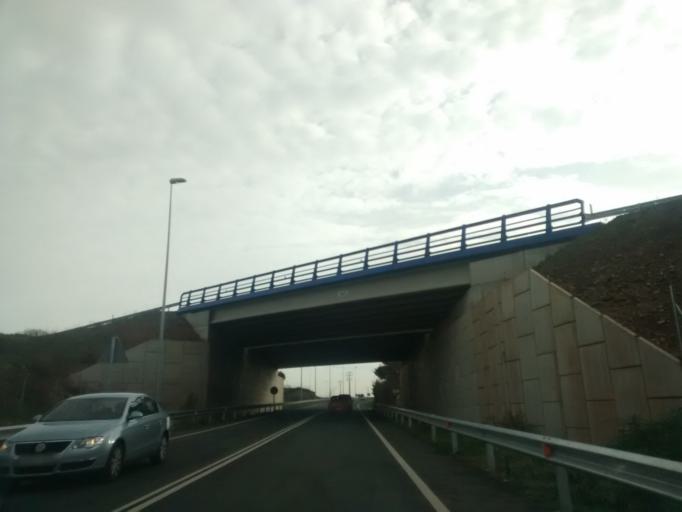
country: ES
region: Navarre
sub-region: Provincia de Navarra
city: Viana
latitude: 42.4741
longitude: -2.3564
